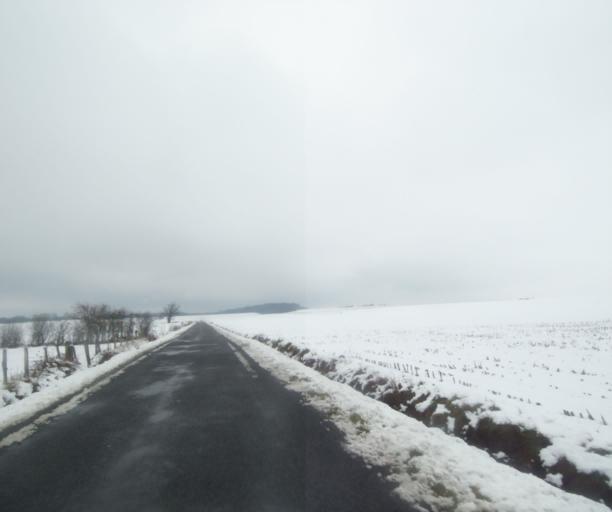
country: FR
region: Champagne-Ardenne
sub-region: Departement de la Haute-Marne
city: Montier-en-Der
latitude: 48.4704
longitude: 4.7958
